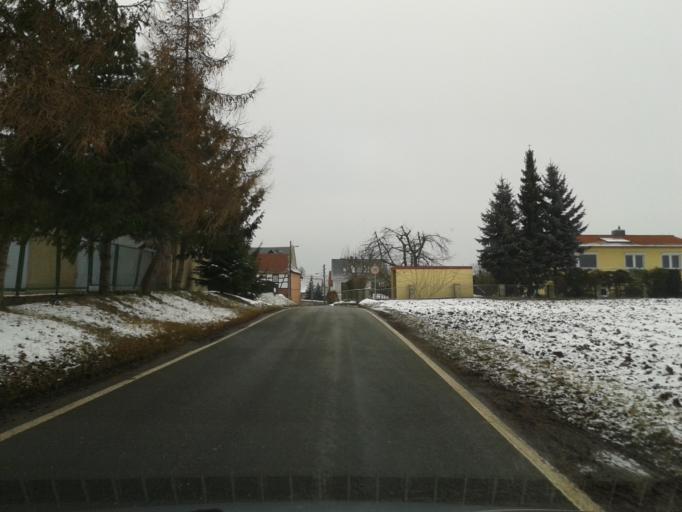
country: DE
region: Thuringia
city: Lehesten
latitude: 50.9713
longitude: 11.5374
